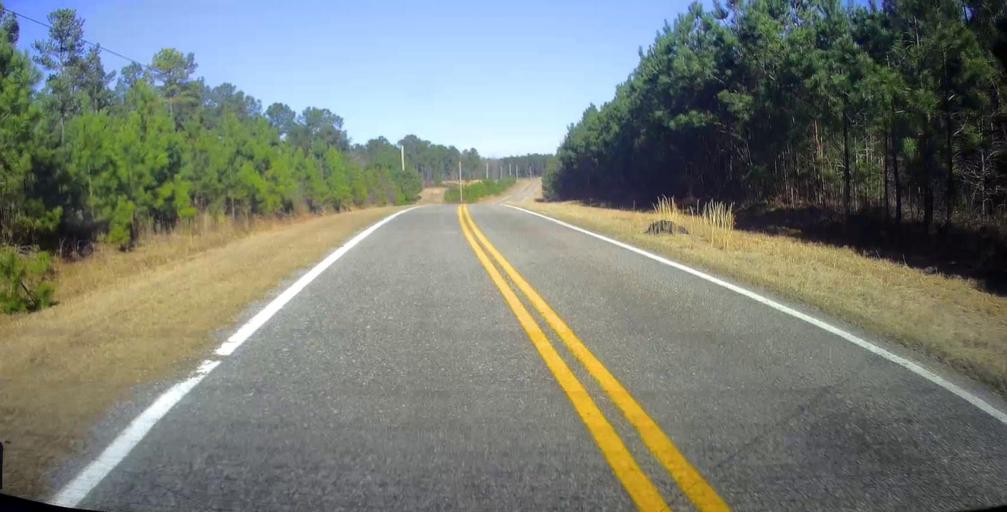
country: US
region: Georgia
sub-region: Peach County
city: Fort Valley
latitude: 32.6346
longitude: -83.9383
